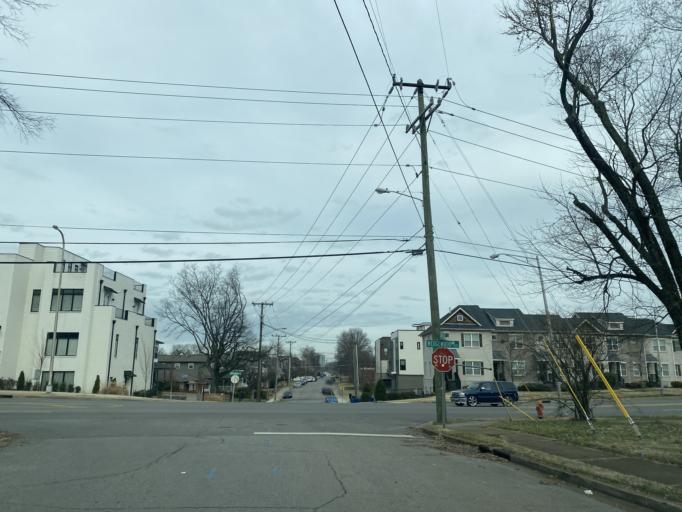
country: US
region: Tennessee
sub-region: Davidson County
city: Nashville
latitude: 36.1357
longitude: -86.7908
